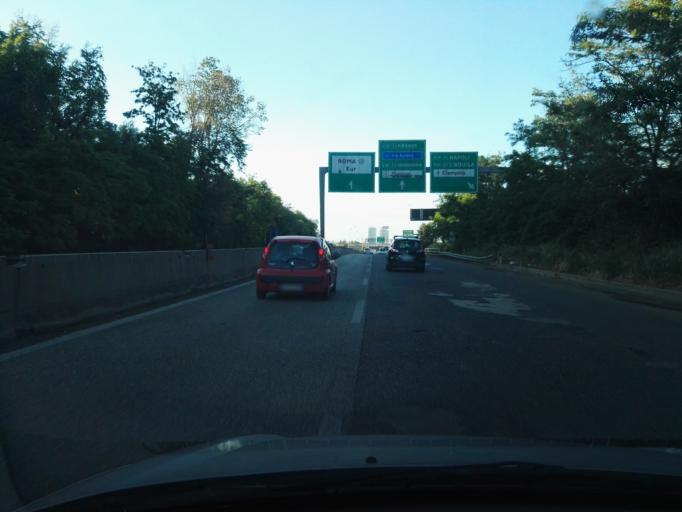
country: IT
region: Latium
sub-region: Citta metropolitana di Roma Capitale
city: Selcetta
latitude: 41.7969
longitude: 12.4530
